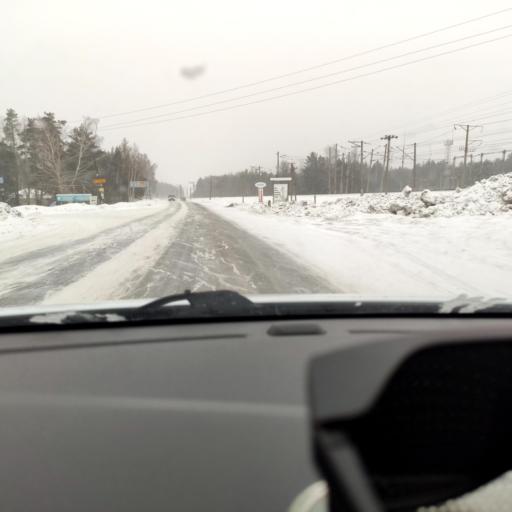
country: RU
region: Tatarstan
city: Vysokaya Gora
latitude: 55.8920
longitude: 49.2487
